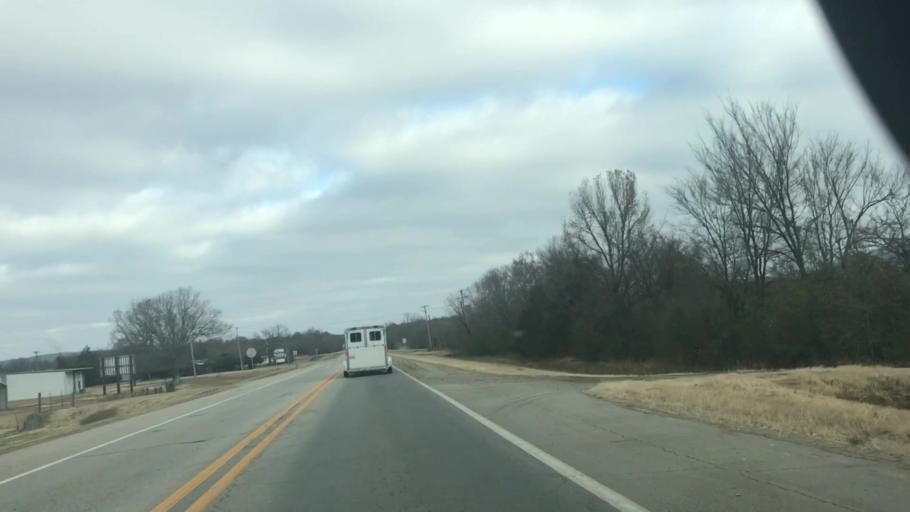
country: US
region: Arkansas
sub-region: Scott County
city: Waldron
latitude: 34.9063
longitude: -94.1073
